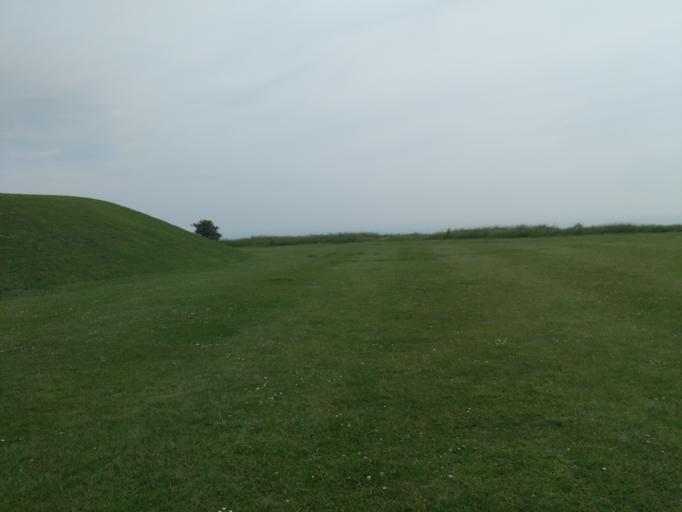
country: GB
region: England
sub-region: Kent
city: Folkestone
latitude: 51.0983
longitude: 1.2063
